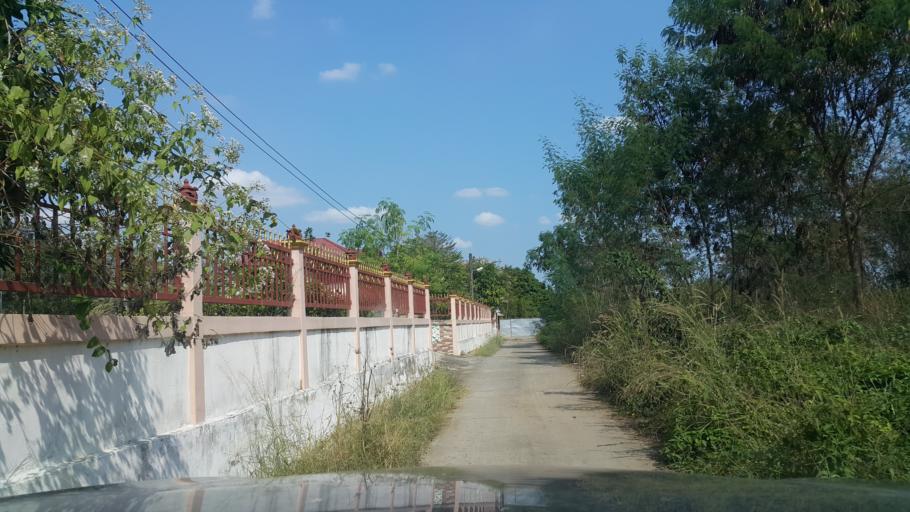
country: TH
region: Sukhothai
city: Thung Saliam
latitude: 17.3198
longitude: 99.5520
